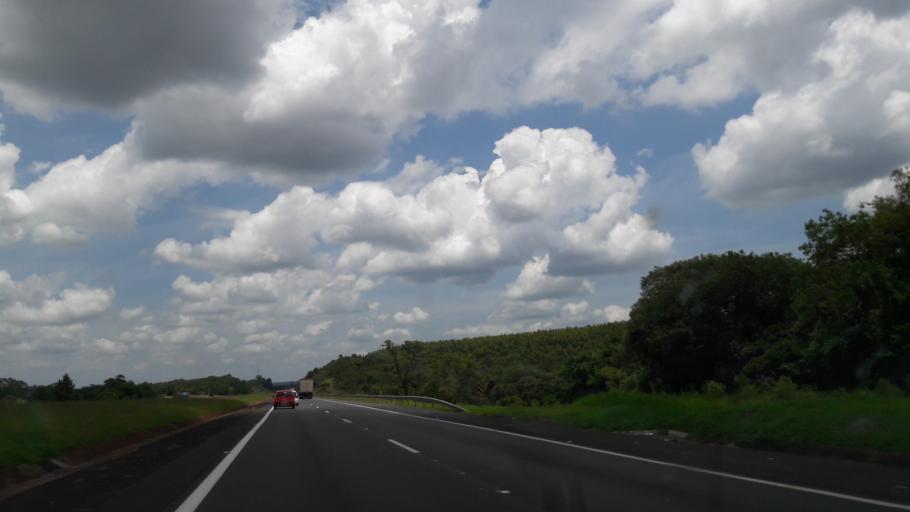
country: BR
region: Sao Paulo
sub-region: Itatinga
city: Itatinga
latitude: -23.0651
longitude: -48.5574
